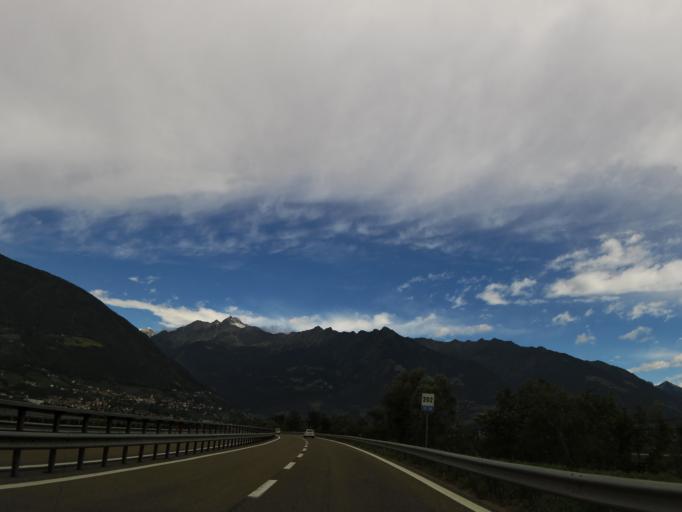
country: IT
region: Trentino-Alto Adige
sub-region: Bolzano
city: Sinigo
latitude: 46.6387
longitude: 11.1696
